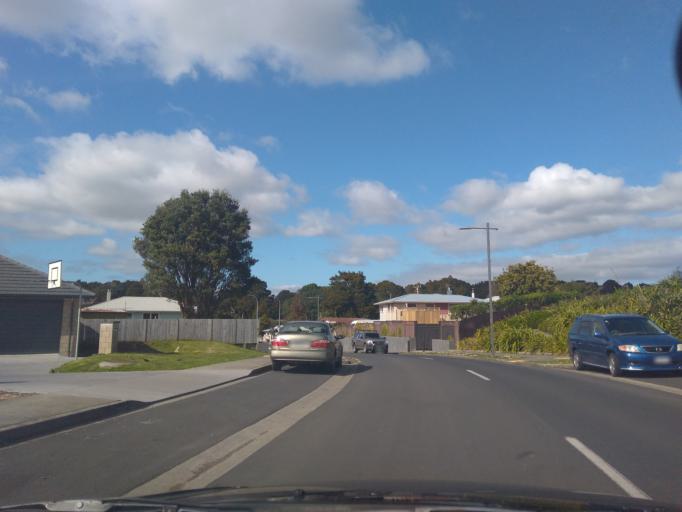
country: NZ
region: Northland
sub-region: Whangarei
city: Whangarei
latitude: -35.6791
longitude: 174.3170
